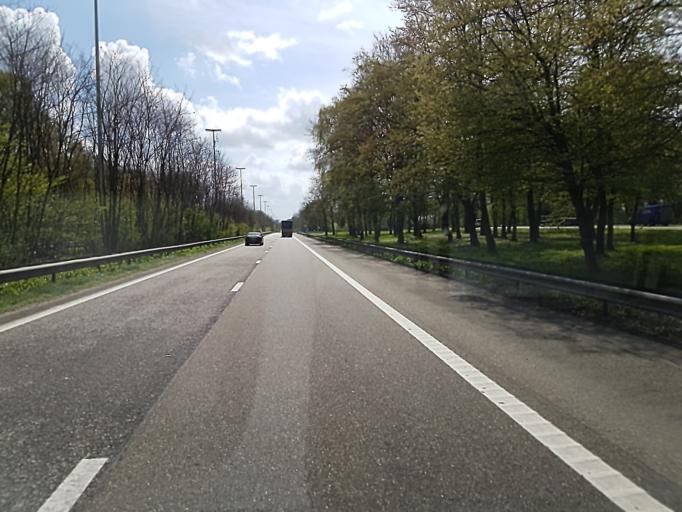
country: BE
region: Flanders
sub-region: Provincie Limburg
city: Hoeselt
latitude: 50.8364
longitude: 5.5086
